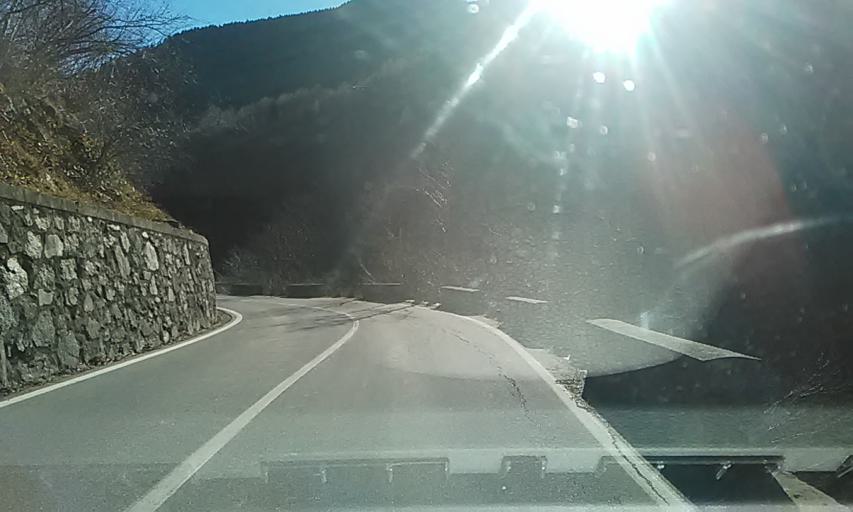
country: IT
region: Piedmont
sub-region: Provincia di Vercelli
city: Rimasco
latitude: 45.8454
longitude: 8.0661
